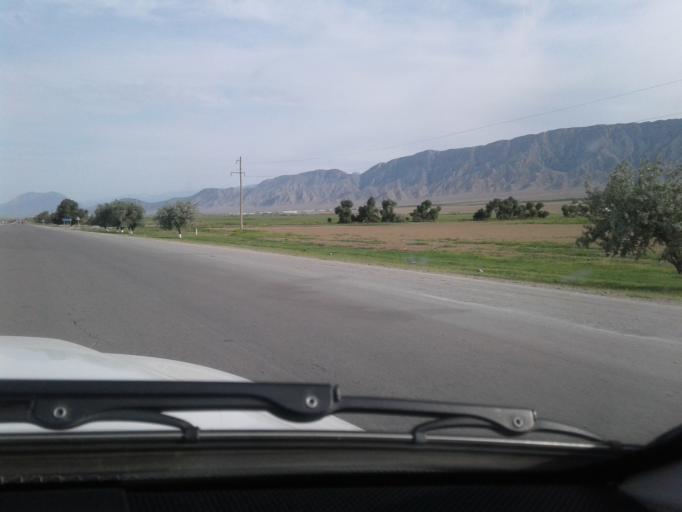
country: TM
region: Ahal
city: Arcabil
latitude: 38.2074
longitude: 57.8177
